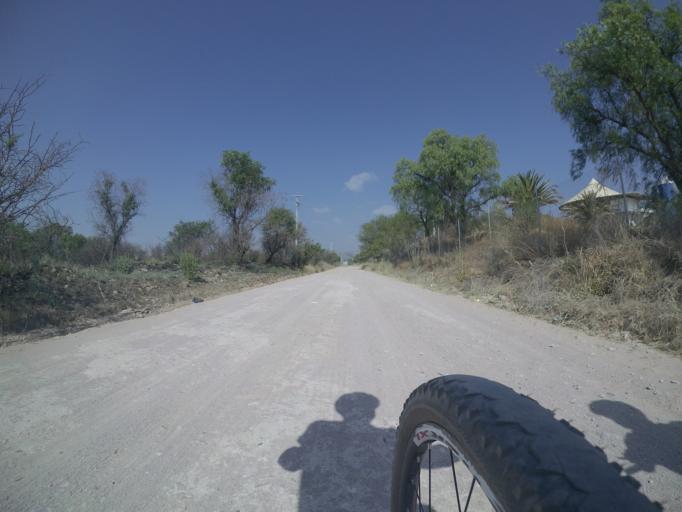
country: MX
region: Aguascalientes
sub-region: Jesus Maria
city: Paseos de las Haciendas [Fraccionamiento]
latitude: 21.9986
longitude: -102.3404
